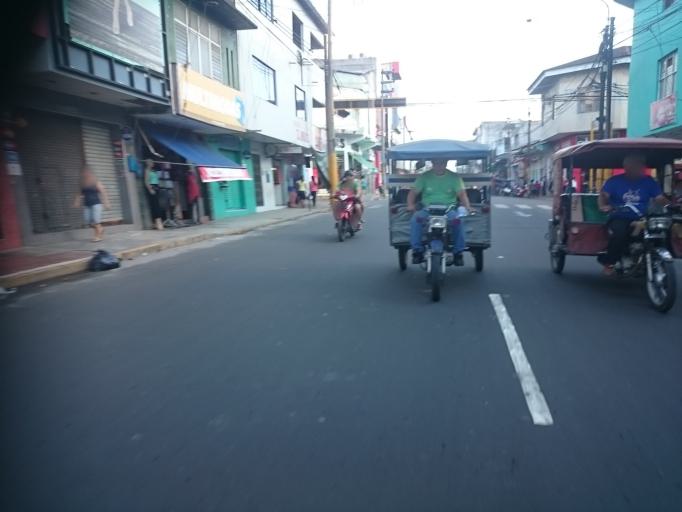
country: PE
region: Loreto
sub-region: Provincia de Maynas
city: Iquitos
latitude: -3.7564
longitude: -73.2479
